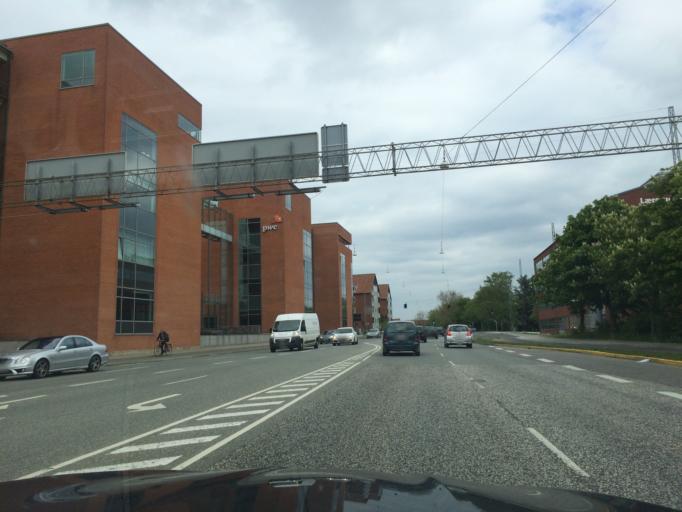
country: DK
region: Central Jutland
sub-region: Arhus Kommune
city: Arhus
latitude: 56.1717
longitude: 10.2054
